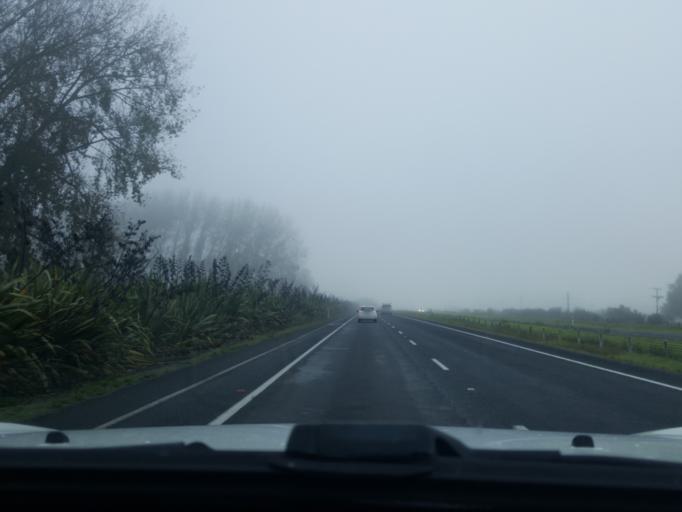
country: NZ
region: Waikato
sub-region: Waikato District
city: Te Kauwhata
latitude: -37.4561
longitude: 175.1542
